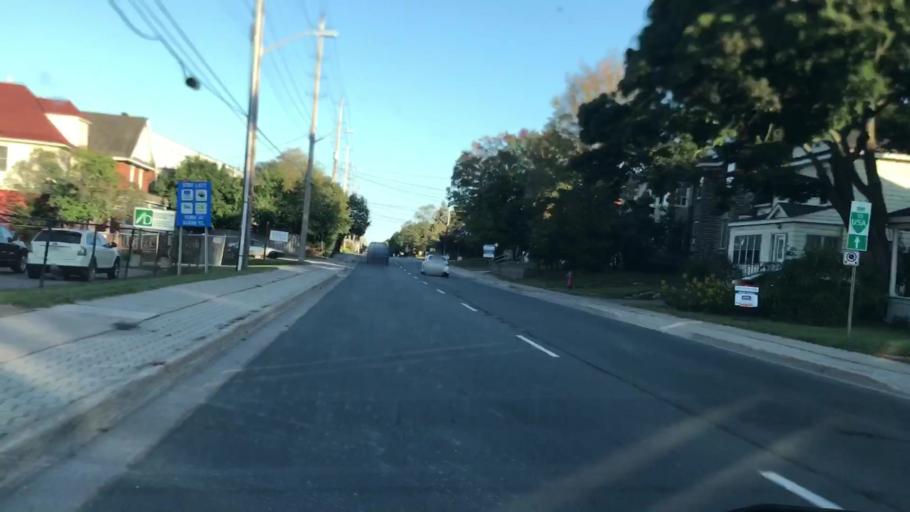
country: CA
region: Ontario
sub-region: Algoma
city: Sault Ste. Marie
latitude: 46.5099
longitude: -84.3259
